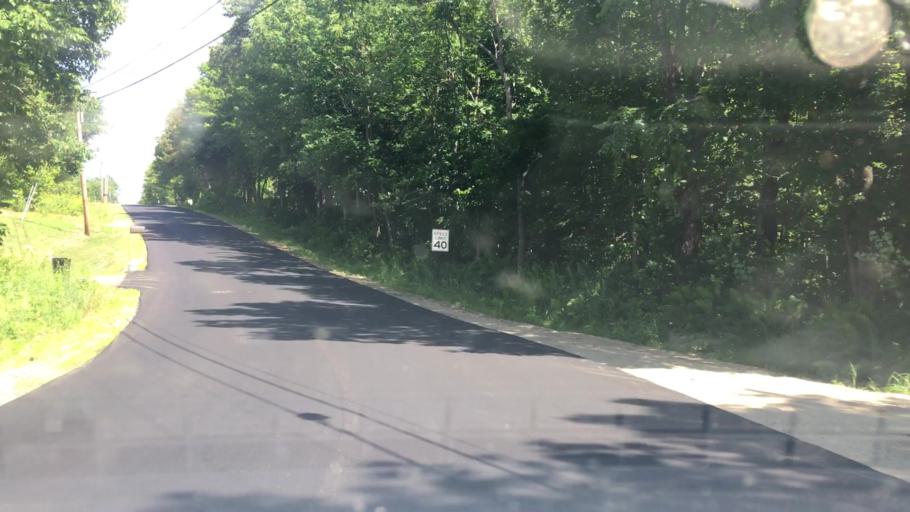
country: US
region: Maine
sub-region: Franklin County
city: Wilton
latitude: 44.5754
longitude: -70.1645
